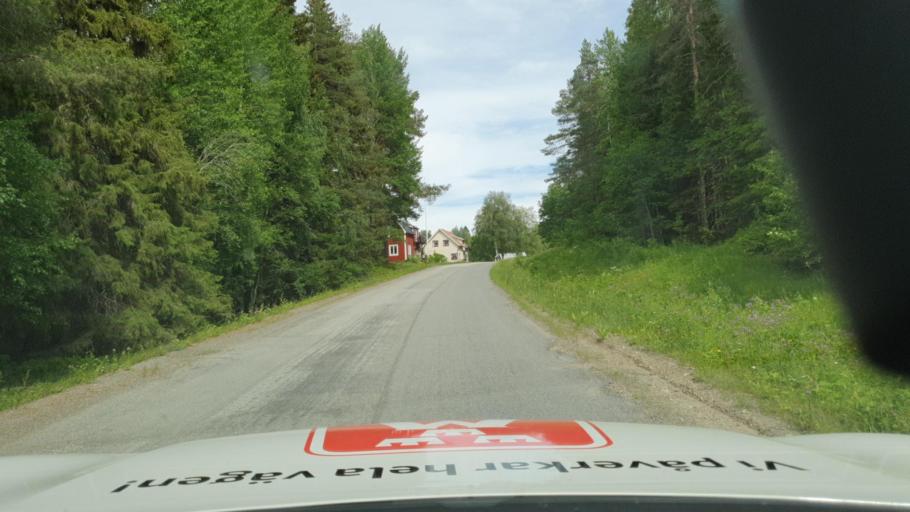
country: SE
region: Vaesterbotten
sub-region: Skelleftea Kommun
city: Burtraesk
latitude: 64.4844
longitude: 20.5350
